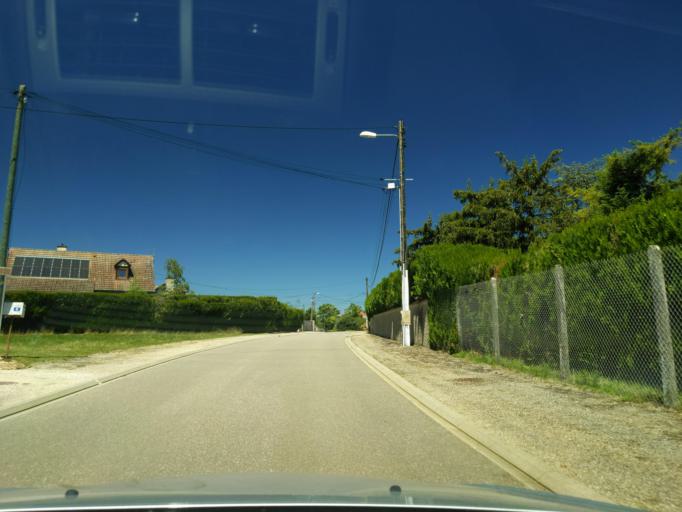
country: FR
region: Bourgogne
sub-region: Departement de la Cote-d'Or
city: Saint-Julien
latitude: 47.4370
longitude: 5.1008
